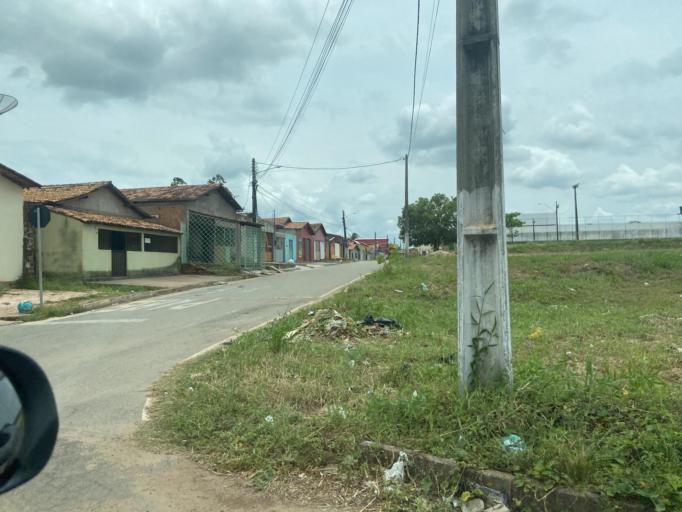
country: BR
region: Para
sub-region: Maraba
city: Maraba
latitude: -5.3497
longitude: -49.0761
